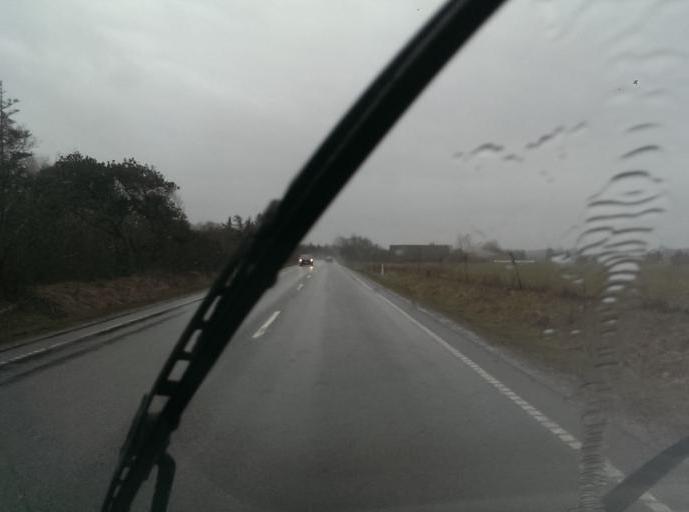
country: DK
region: Central Jutland
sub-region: Ringkobing-Skjern Kommune
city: Tarm
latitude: 55.8758
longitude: 8.5067
